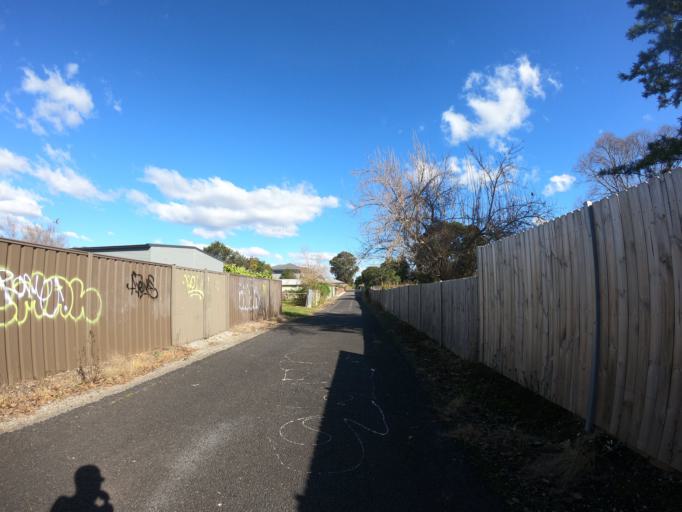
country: AU
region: New South Wales
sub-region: Hawkesbury
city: South Windsor
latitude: -33.6205
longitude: 150.8068
